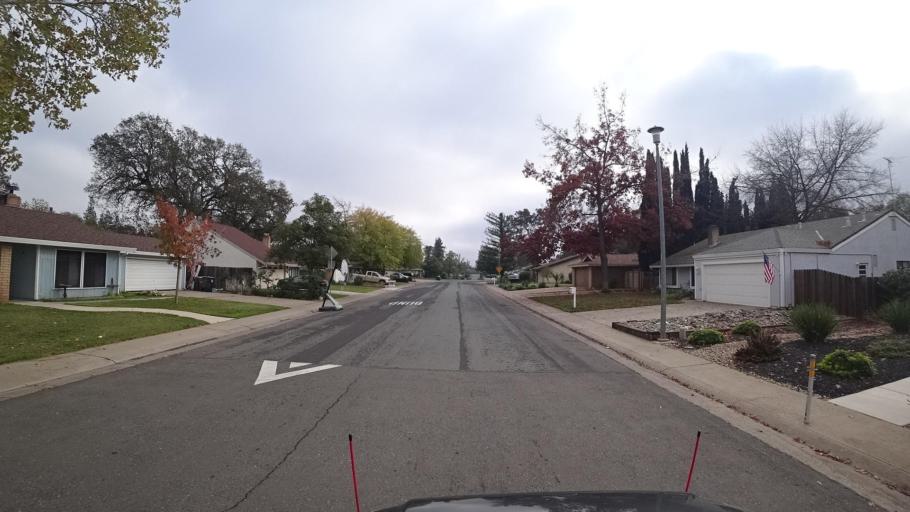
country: US
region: California
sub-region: Sacramento County
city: Elk Grove
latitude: 38.4122
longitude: -121.3663
